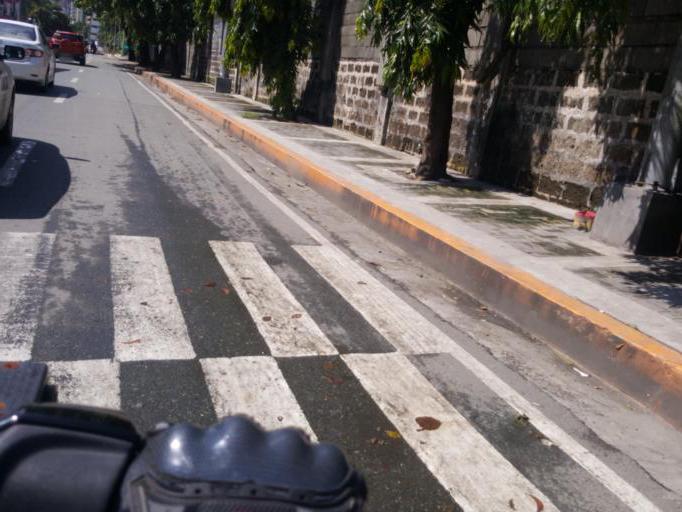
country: PH
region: Metro Manila
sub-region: City of Manila
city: Port Area
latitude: 14.5709
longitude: 120.9825
